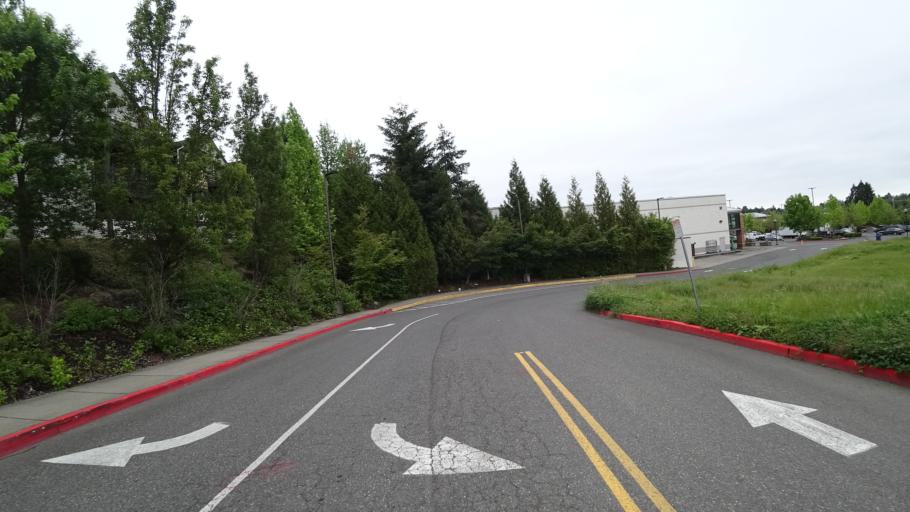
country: US
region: Oregon
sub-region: Washington County
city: Bethany
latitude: 45.5595
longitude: -122.8673
